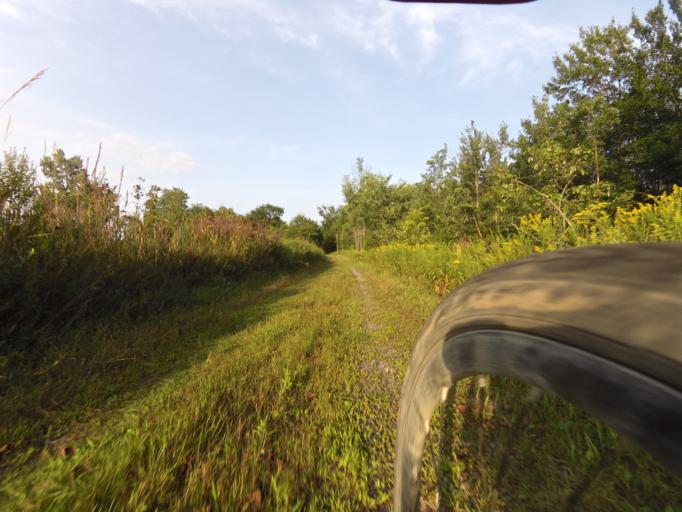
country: CA
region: Ontario
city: Gananoque
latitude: 44.5590
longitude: -76.3703
